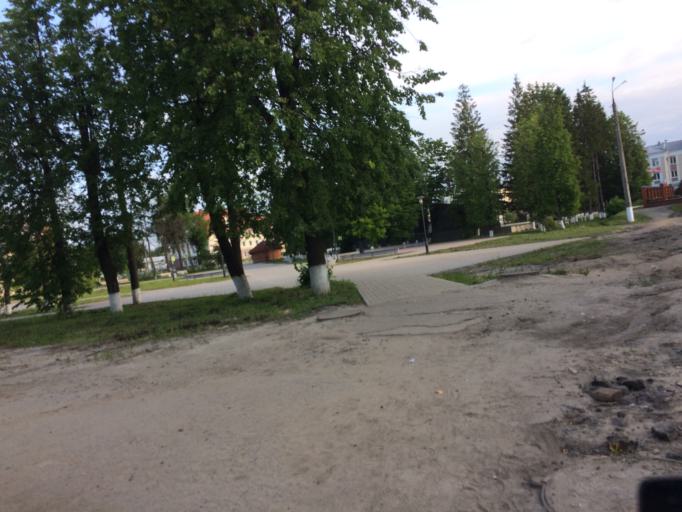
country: RU
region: Mariy-El
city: Medvedevo
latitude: 56.6316
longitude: 47.8058
